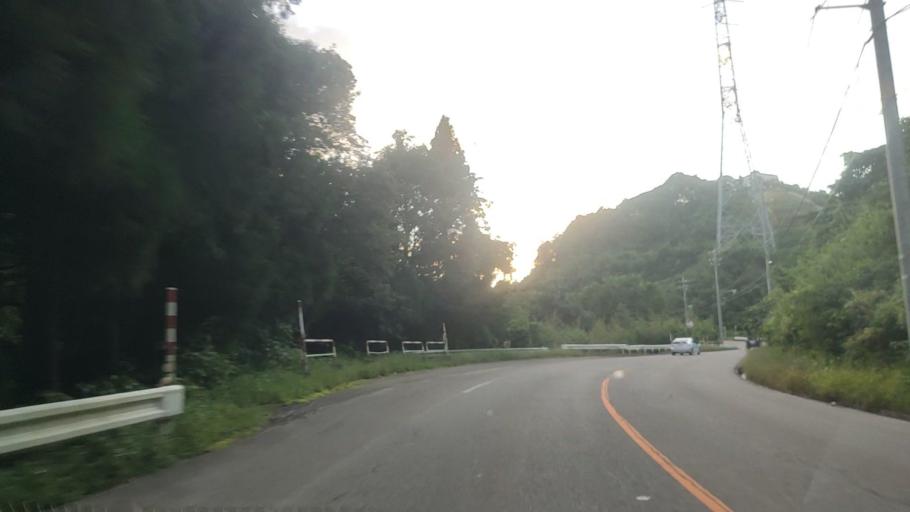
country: JP
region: Toyama
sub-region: Oyabe Shi
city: Oyabe
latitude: 36.6295
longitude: 136.8135
